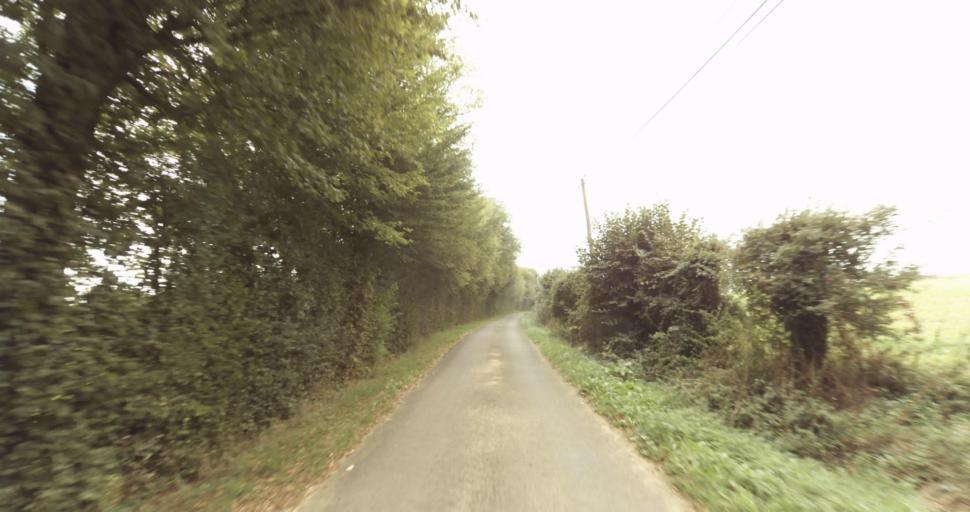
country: FR
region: Lower Normandy
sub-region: Departement de l'Orne
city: Gace
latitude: 48.7276
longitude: 0.3168
